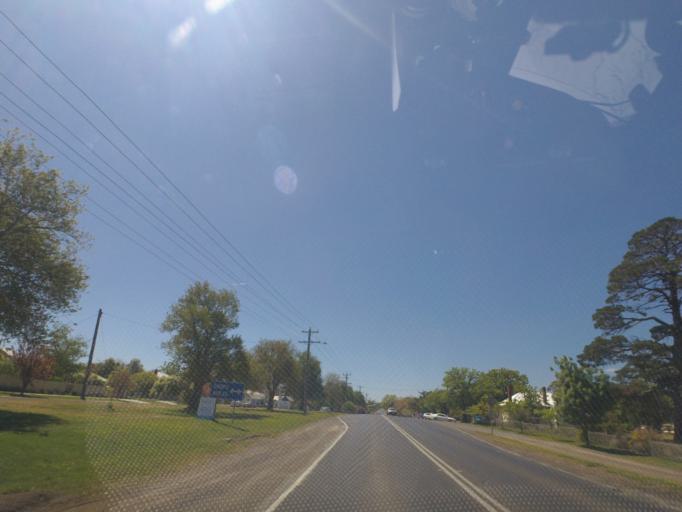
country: AU
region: Victoria
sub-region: Hume
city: Sunbury
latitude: -37.4640
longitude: 144.6752
